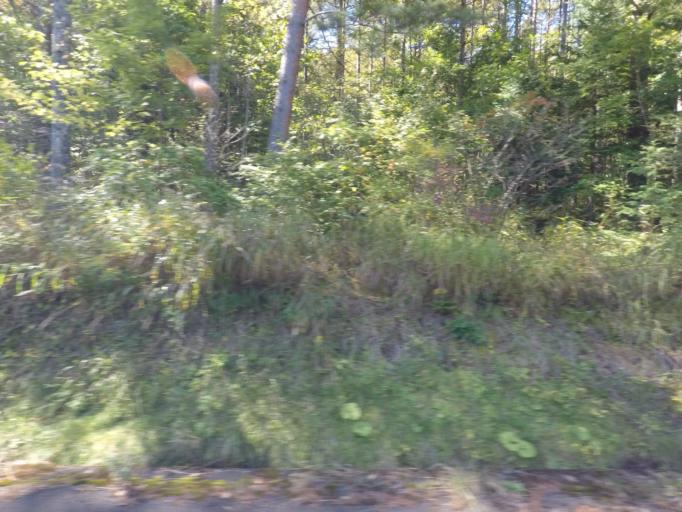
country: JP
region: Nagano
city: Shiojiri
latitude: 35.9973
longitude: 137.7344
